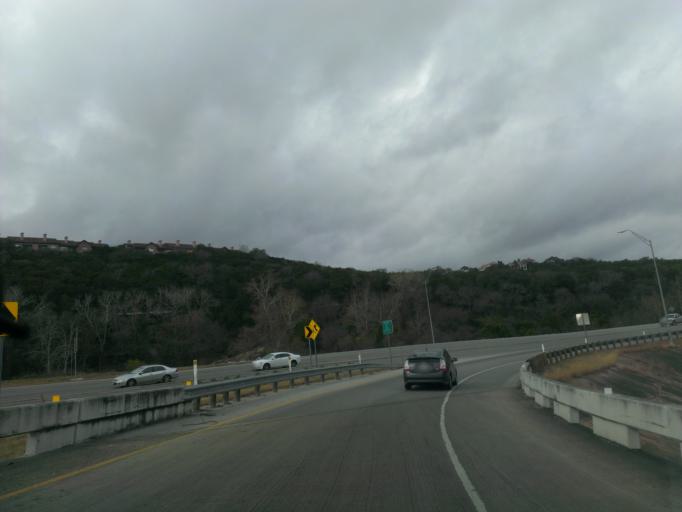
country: US
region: Texas
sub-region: Travis County
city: West Lake Hills
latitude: 30.3599
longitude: -97.7922
